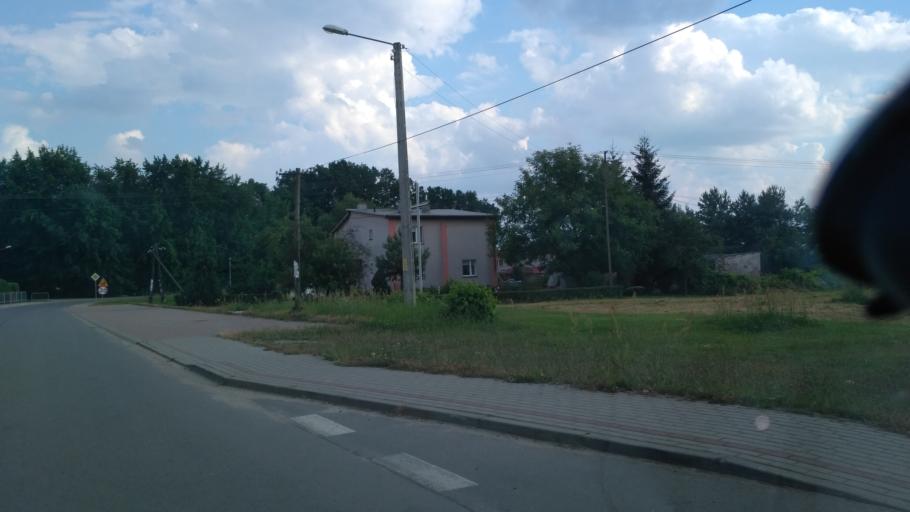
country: PL
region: Subcarpathian Voivodeship
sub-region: Powiat rzeszowski
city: Wysoka Glogowska
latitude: 50.1582
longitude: 22.0216
